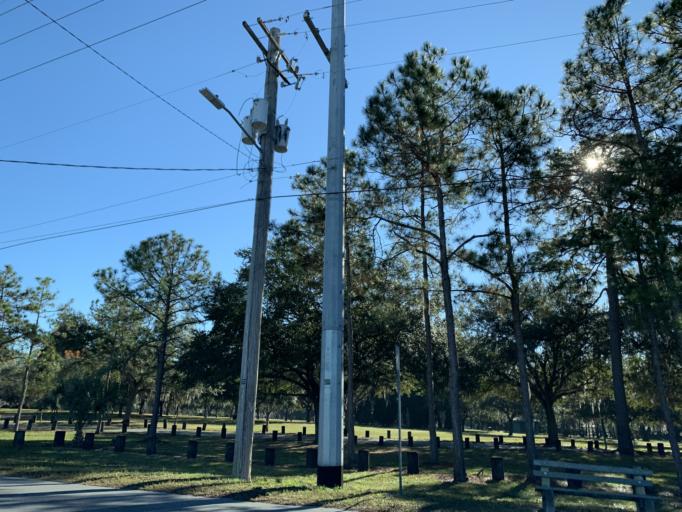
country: US
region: Florida
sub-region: Hillsborough County
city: University
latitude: 28.0275
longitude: -82.4324
